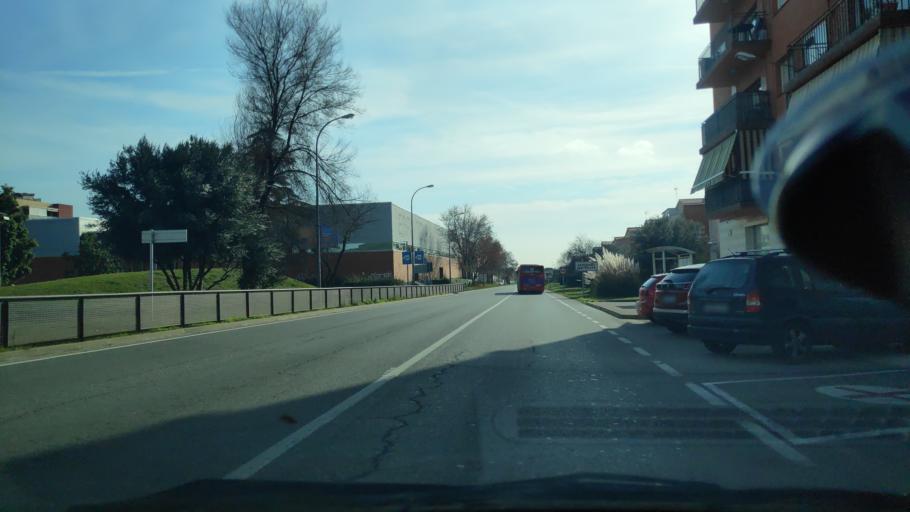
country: ES
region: Catalonia
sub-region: Provincia de Barcelona
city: Castellar del Valles
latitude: 41.6097
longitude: 2.0839
